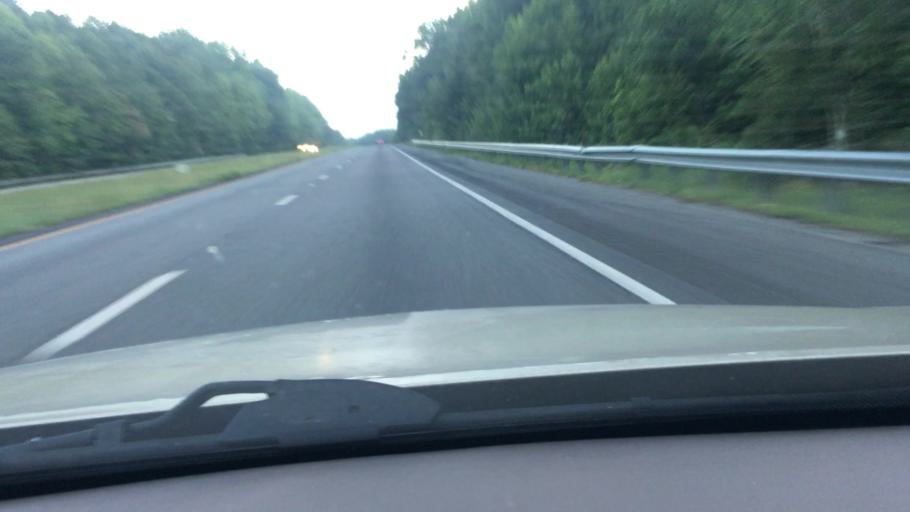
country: US
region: South Carolina
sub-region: Lexington County
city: Irmo
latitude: 34.1262
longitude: -81.2027
